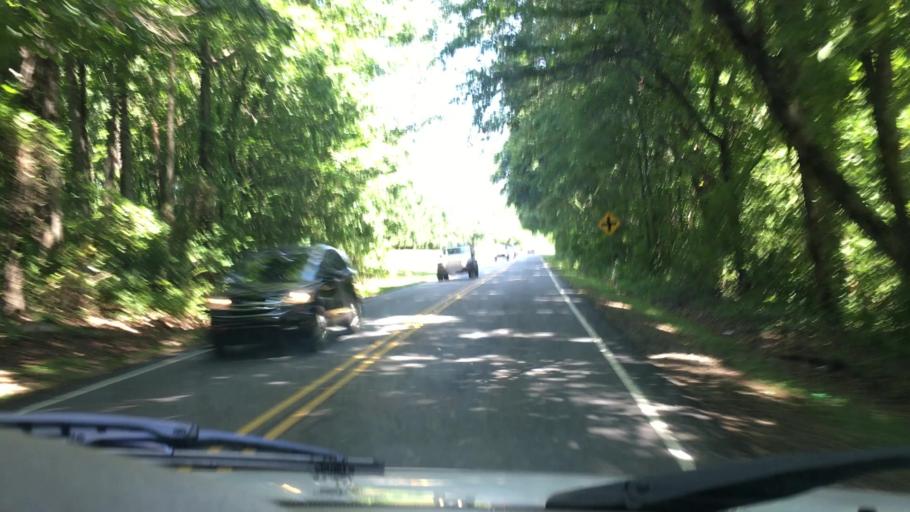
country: US
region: North Carolina
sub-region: Mecklenburg County
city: Huntersville
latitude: 35.3865
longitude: -80.9205
